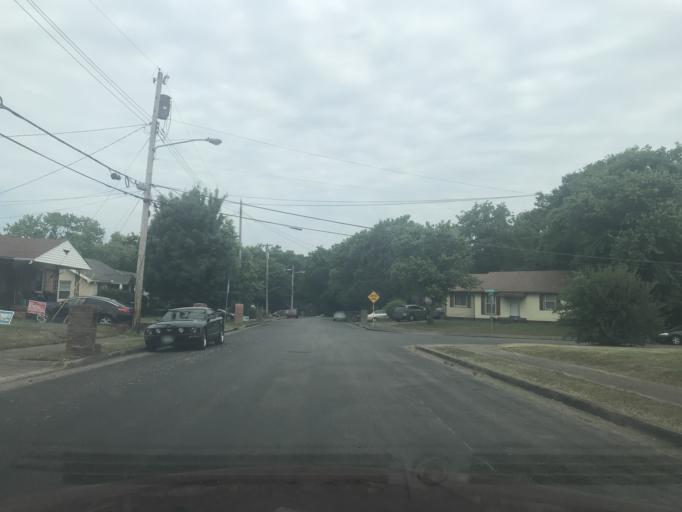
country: US
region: Tennessee
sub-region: Davidson County
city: Nashville
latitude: 36.1723
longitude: -86.8149
